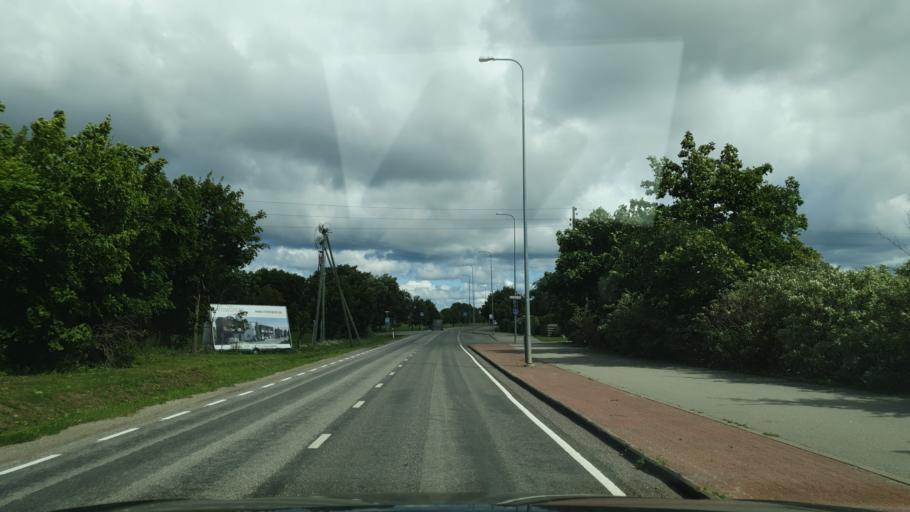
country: EE
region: Harju
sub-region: Viimsi vald
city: Viimsi
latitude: 59.5071
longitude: 24.8484
